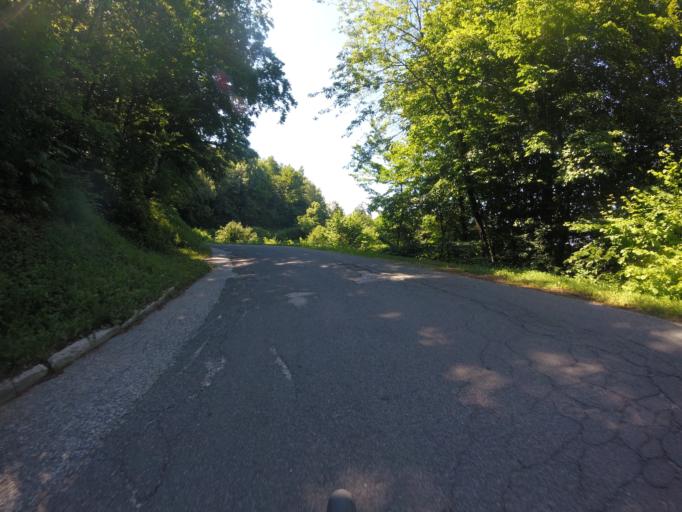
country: SI
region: Kostanjevica na Krki
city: Kostanjevica na Krki
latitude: 45.8034
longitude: 15.4966
